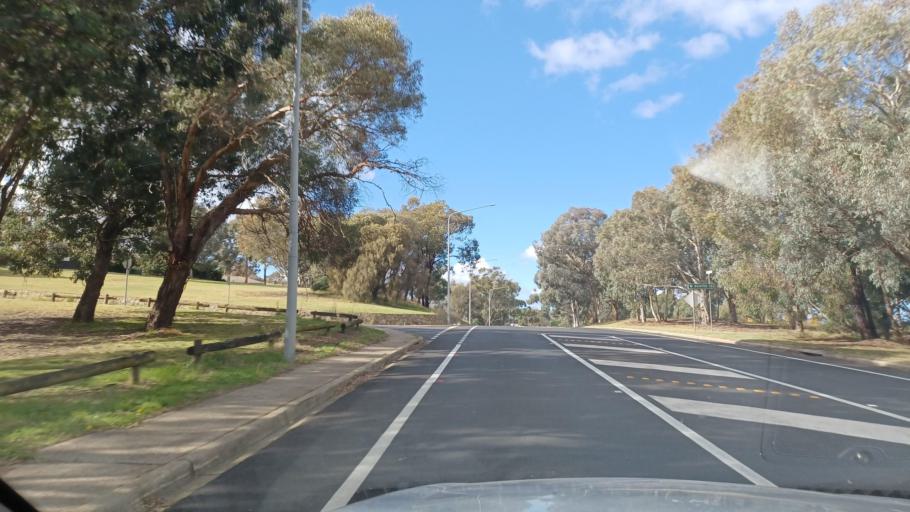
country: AU
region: Australian Capital Territory
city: Belconnen
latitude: -35.2029
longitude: 149.0532
